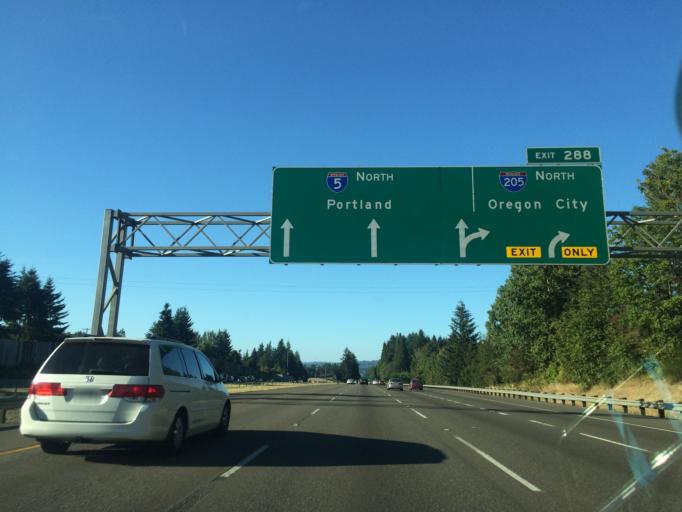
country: US
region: Oregon
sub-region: Washington County
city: Tualatin
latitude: 45.3566
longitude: -122.7627
